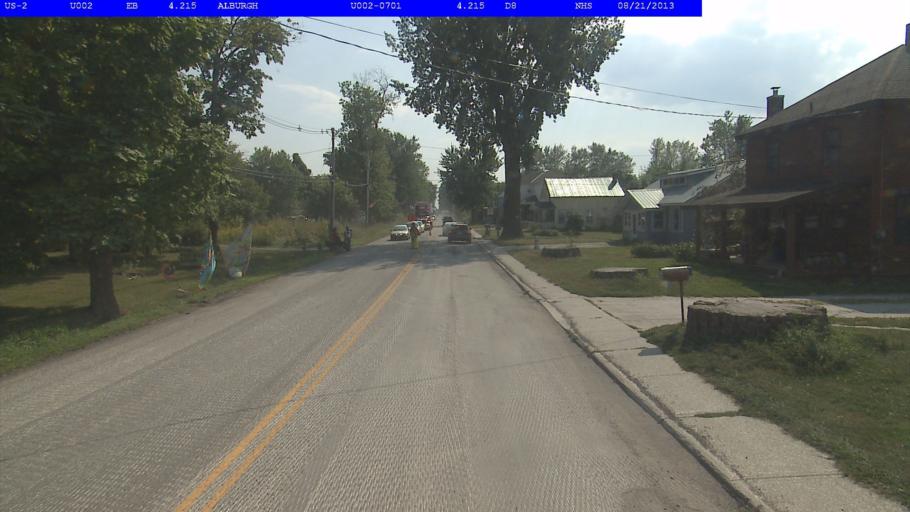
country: US
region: New York
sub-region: Clinton County
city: Rouses Point
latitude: 44.9736
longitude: -73.3017
